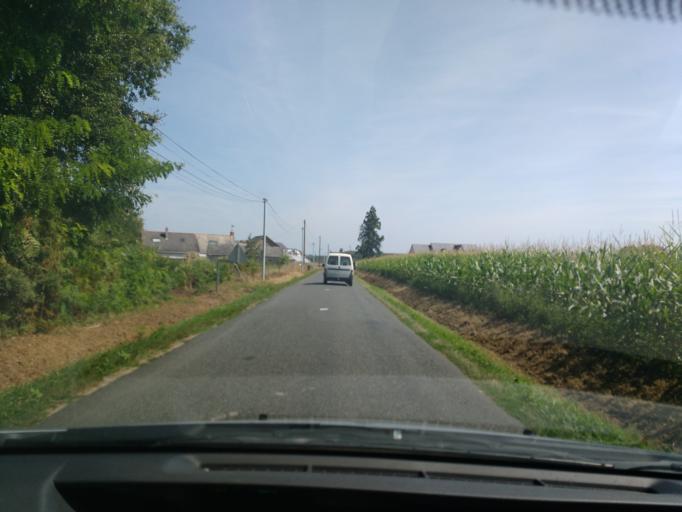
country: FR
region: Pays de la Loire
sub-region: Departement de Maine-et-Loire
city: Beaufort-en-Vallee
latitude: 47.4899
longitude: -0.2125
